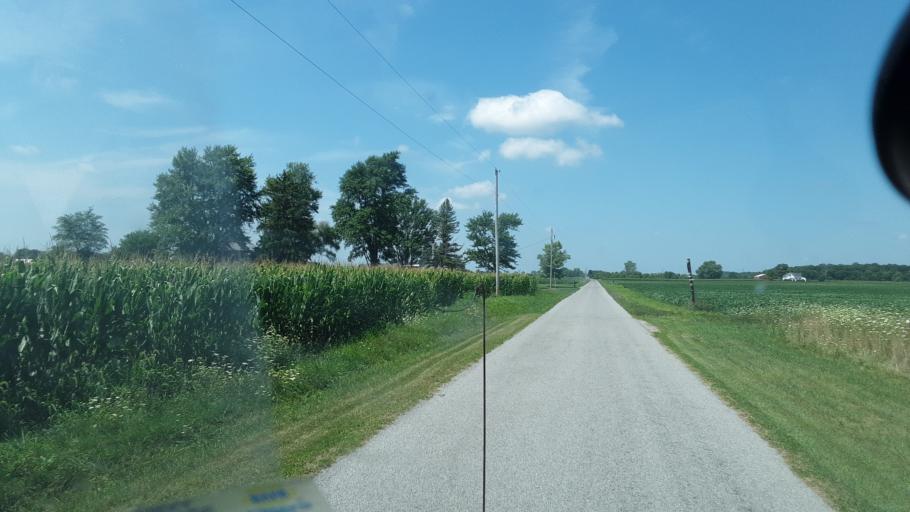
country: US
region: Ohio
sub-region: Hancock County
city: Findlay
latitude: 40.9715
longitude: -83.5668
